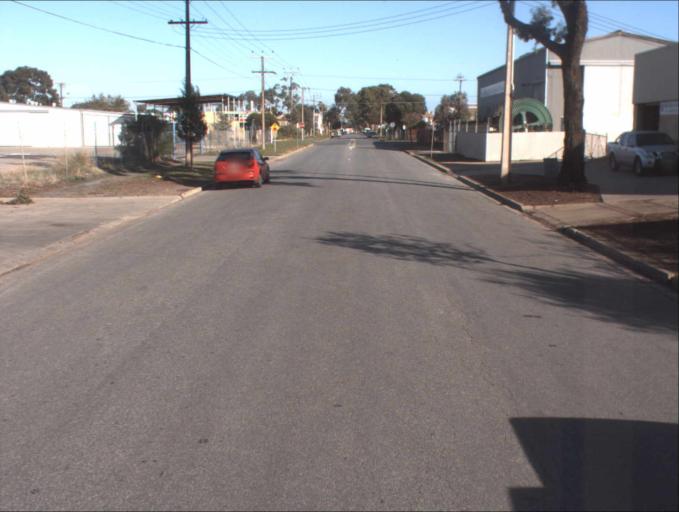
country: AU
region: South Australia
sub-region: Charles Sturt
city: Woodville North
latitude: -34.8457
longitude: 138.5523
